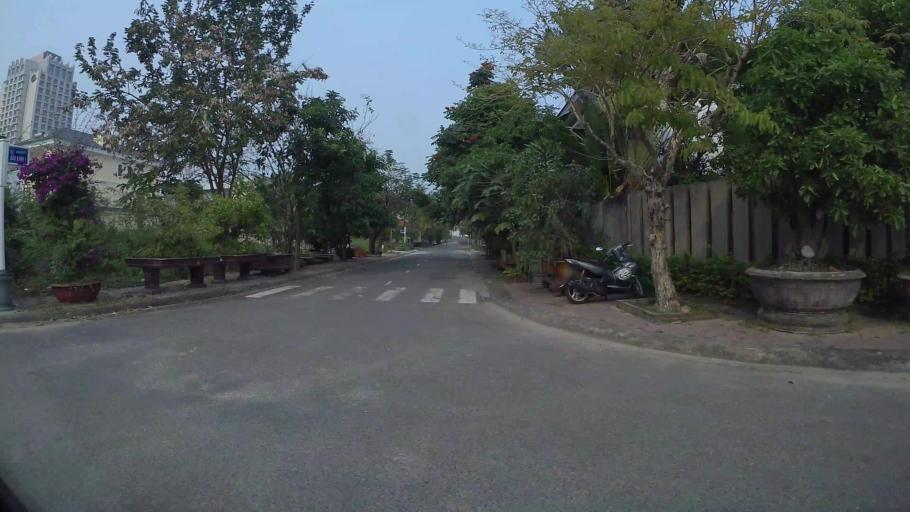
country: VN
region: Da Nang
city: Son Tra
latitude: 16.0460
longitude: 108.2268
